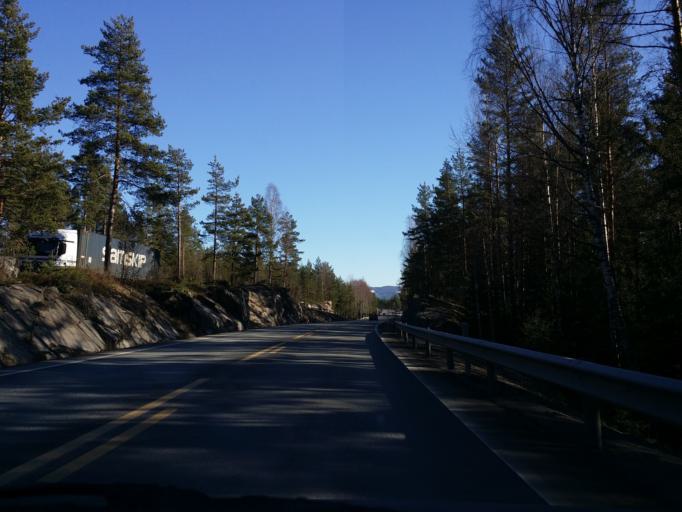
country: NO
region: Buskerud
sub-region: Ringerike
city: Honefoss
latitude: 60.2318
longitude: 10.2326
